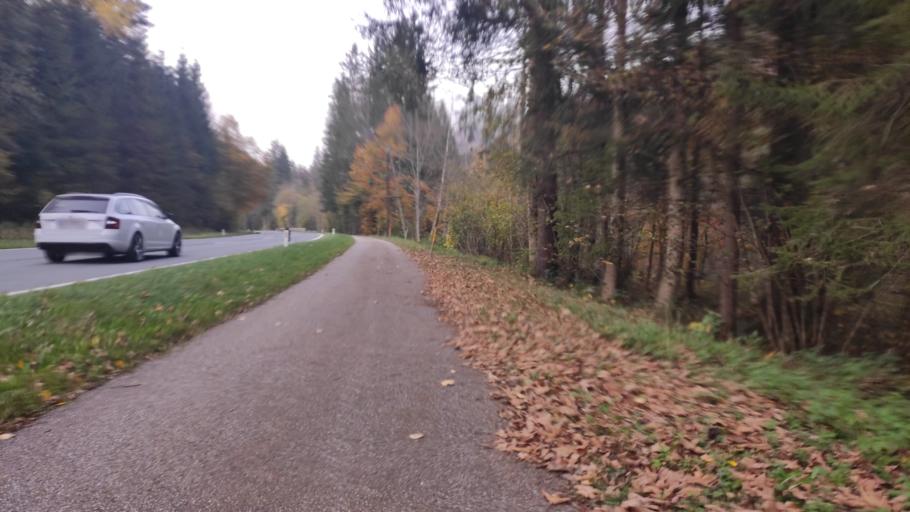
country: AT
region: Salzburg
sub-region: Politischer Bezirk Salzburg-Umgebung
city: Ebenau
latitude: 47.7708
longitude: 13.1820
